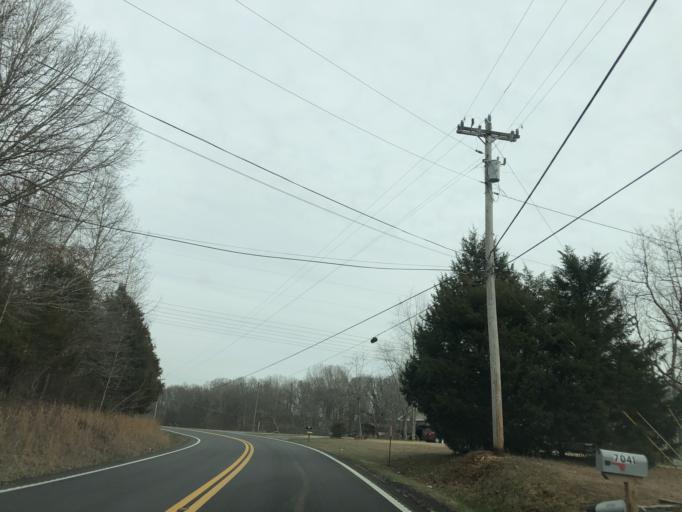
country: US
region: Tennessee
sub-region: Robertson County
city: Greenbrier
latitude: 36.4736
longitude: -86.7512
